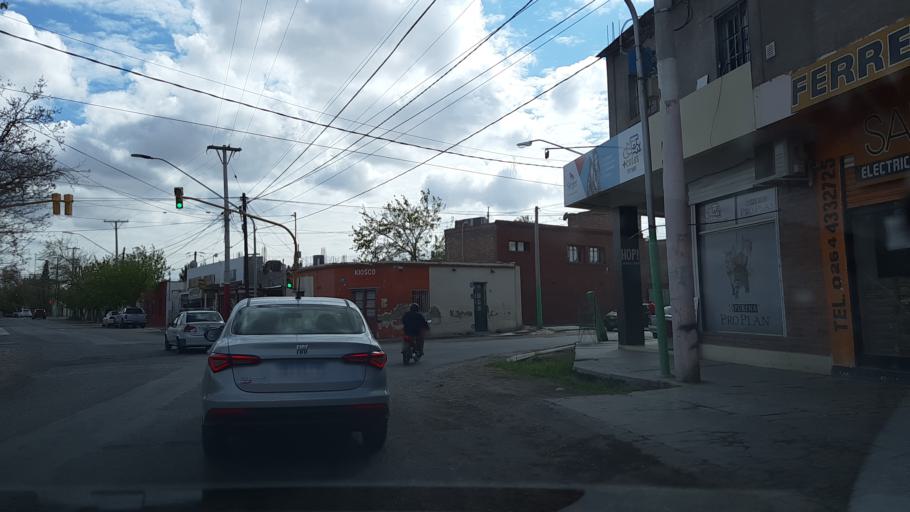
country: AR
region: San Juan
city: San Juan
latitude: -31.5361
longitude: -68.5786
